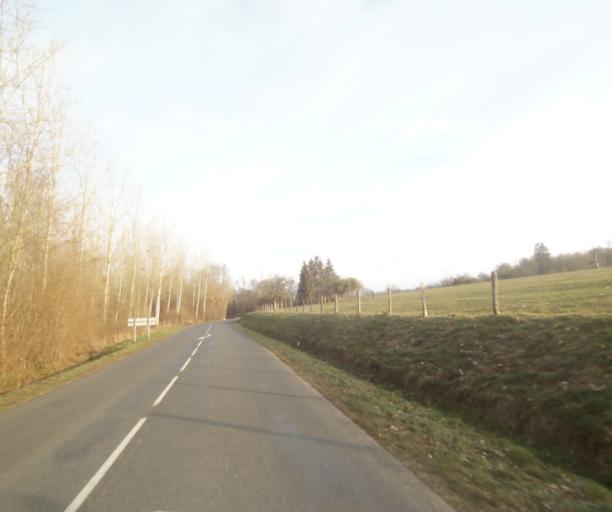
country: FR
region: Champagne-Ardenne
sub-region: Departement de la Marne
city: Sermaize-les-Bains
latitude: 48.7438
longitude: 4.9061
